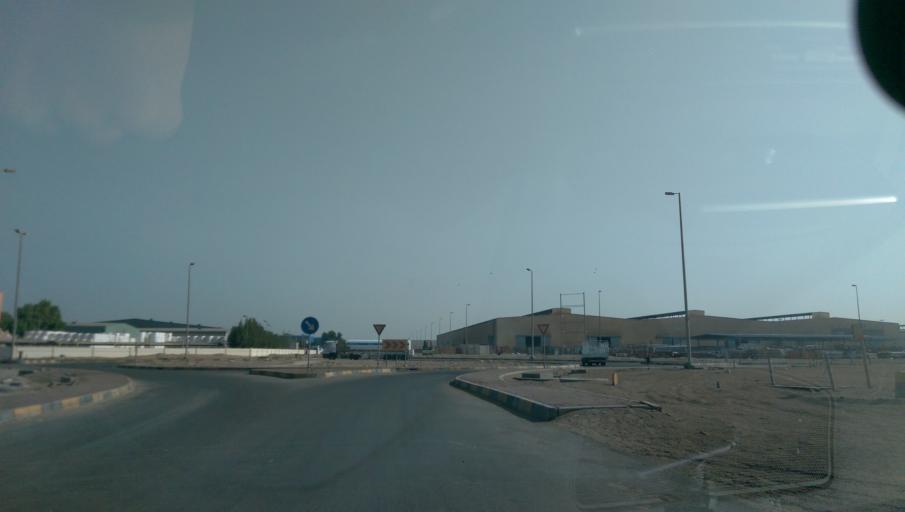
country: AE
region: Abu Dhabi
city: Abu Dhabi
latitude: 24.3277
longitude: 54.4770
